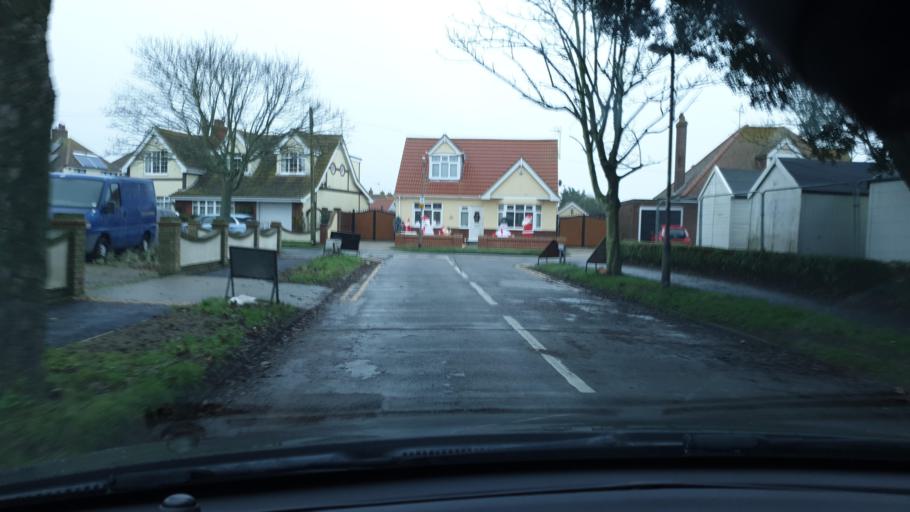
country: GB
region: England
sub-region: Essex
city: Clacton-on-Sea
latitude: 51.8010
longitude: 1.1906
